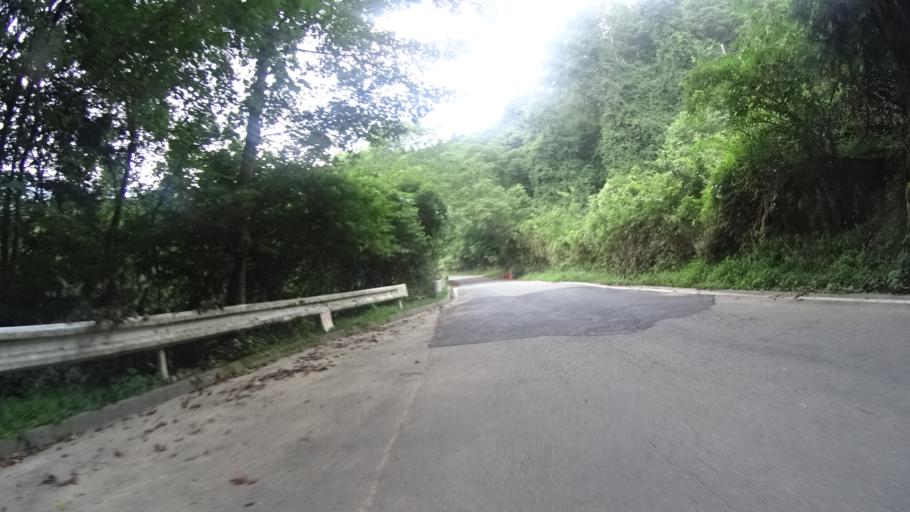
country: JP
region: Yamanashi
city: Enzan
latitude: 35.7903
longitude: 138.6871
